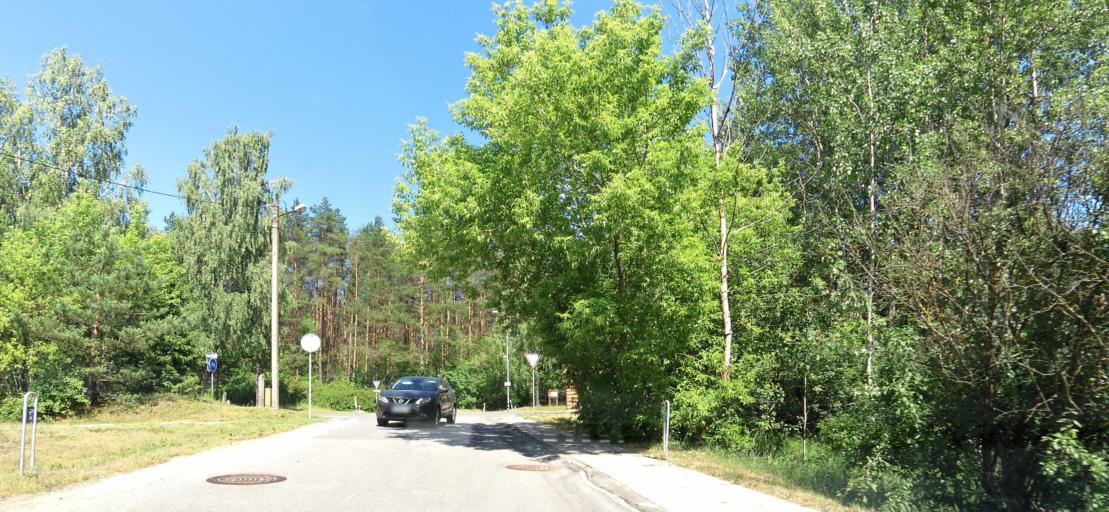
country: LT
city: Nemencine
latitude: 54.7975
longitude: 25.3961
